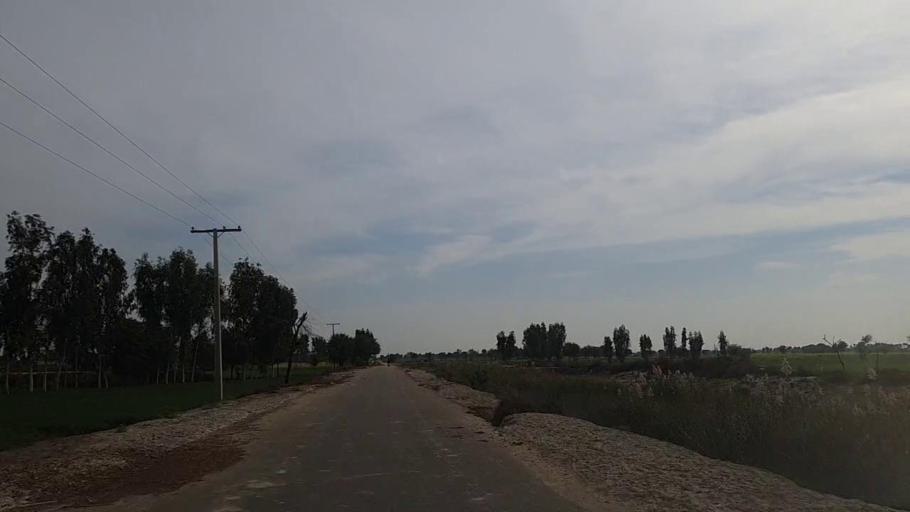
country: PK
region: Sindh
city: Daur
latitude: 26.4254
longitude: 68.4834
